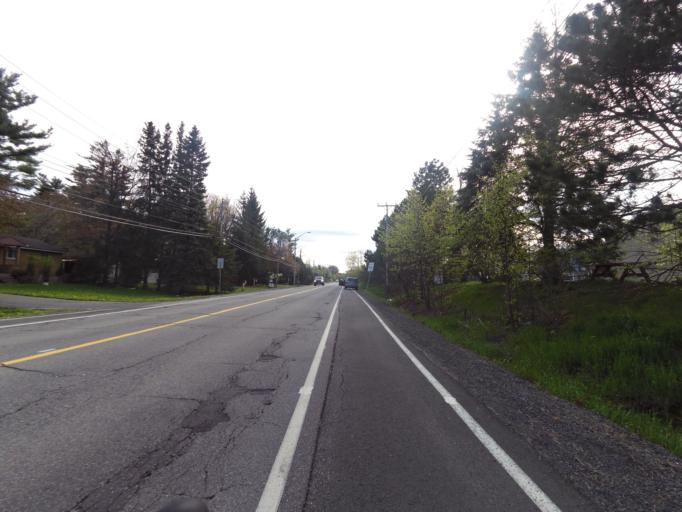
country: CA
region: Ontario
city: Ottawa
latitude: 45.3273
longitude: -75.7102
